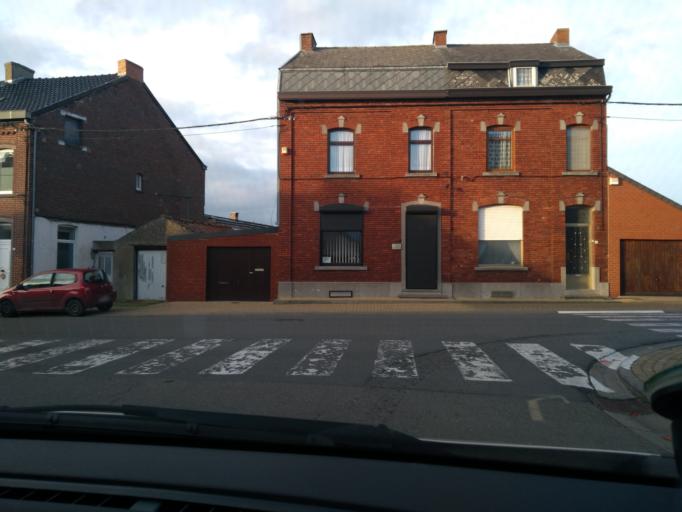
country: BE
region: Wallonia
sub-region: Province du Hainaut
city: Morlanwelz-Mariemont
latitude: 50.4303
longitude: 4.2260
